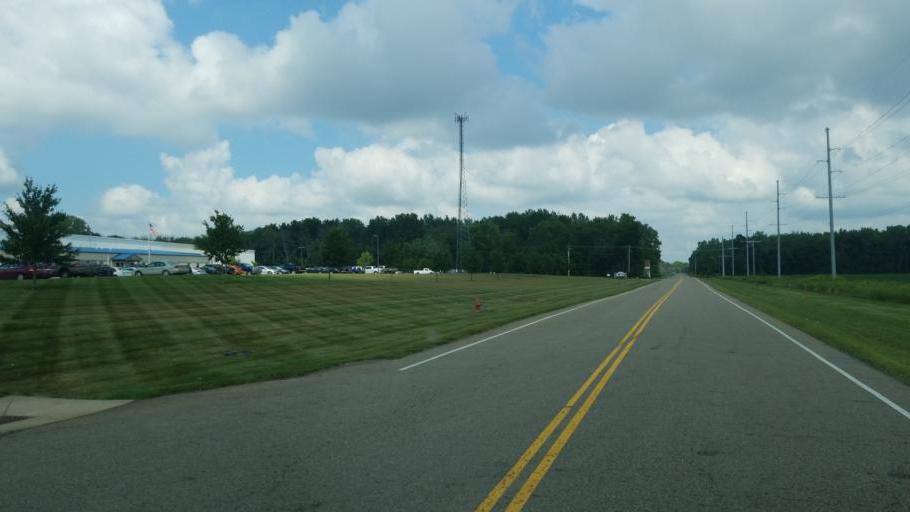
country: US
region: Ohio
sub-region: Knox County
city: Mount Vernon
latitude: 40.3479
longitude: -82.4847
